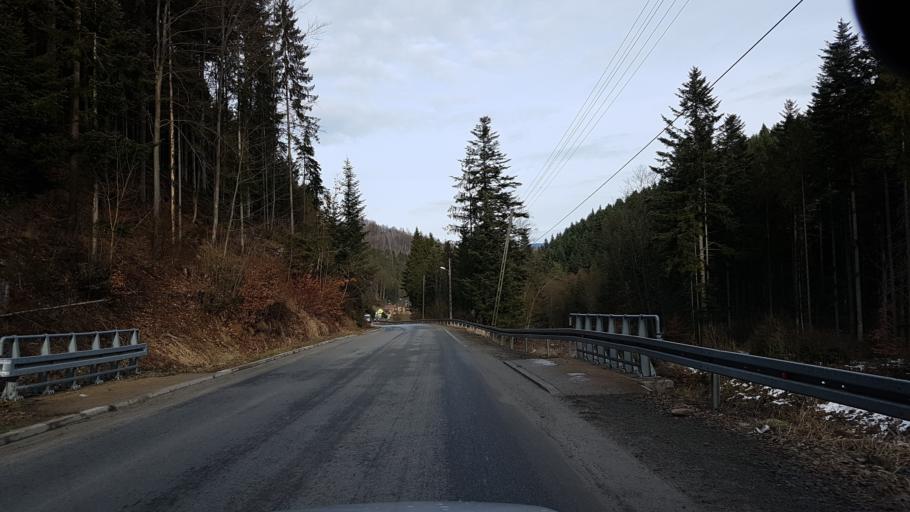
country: PL
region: Lesser Poland Voivodeship
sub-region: Powiat nowosadecki
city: Piwniczna-Zdroj
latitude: 49.4334
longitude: 20.6815
